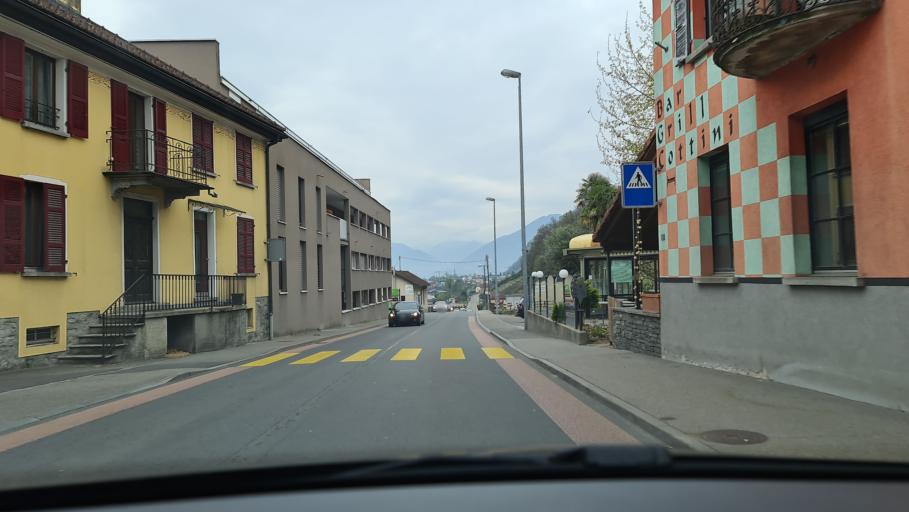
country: CH
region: Ticino
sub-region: Locarno District
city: Cugnasco
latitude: 46.1740
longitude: 8.9401
